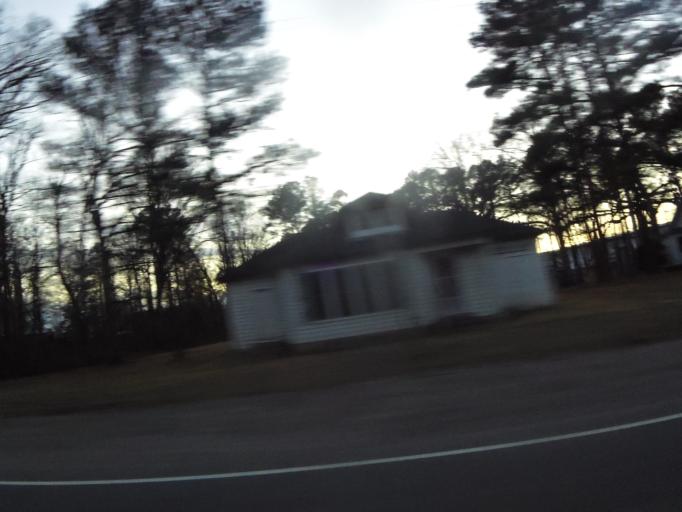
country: US
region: Virginia
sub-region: Sussex County
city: Sussex
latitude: 36.9479
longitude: -77.1714
